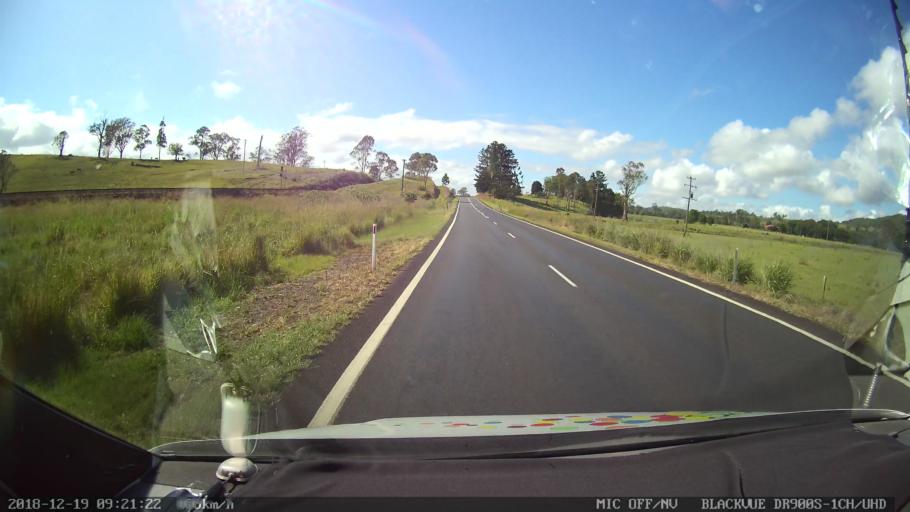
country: AU
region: New South Wales
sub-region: Kyogle
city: Kyogle
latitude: -28.5830
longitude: 152.9821
